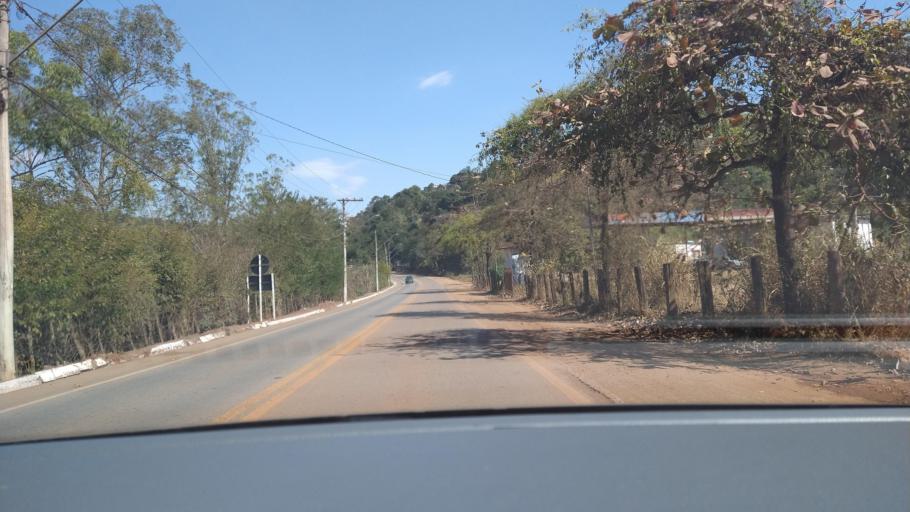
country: BR
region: Minas Gerais
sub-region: Rio Piracicaba
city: Rio Piracicaba
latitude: -19.9206
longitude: -43.1620
